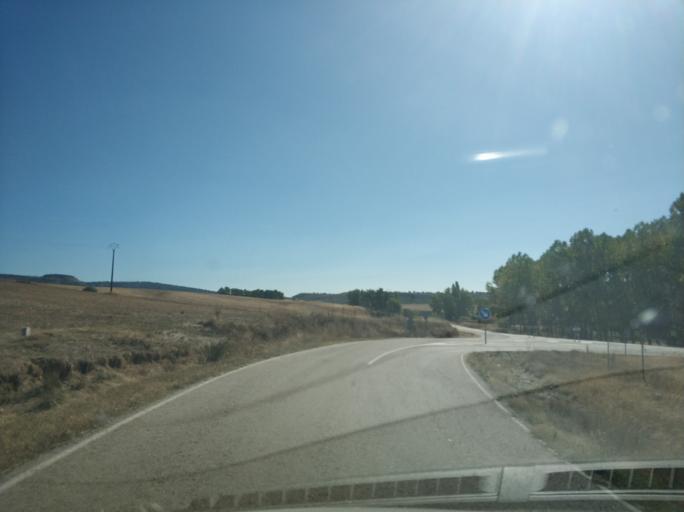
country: ES
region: Castille and Leon
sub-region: Provincia de Soria
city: Santa Maria de las Hoyas
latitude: 41.7700
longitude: -3.1669
